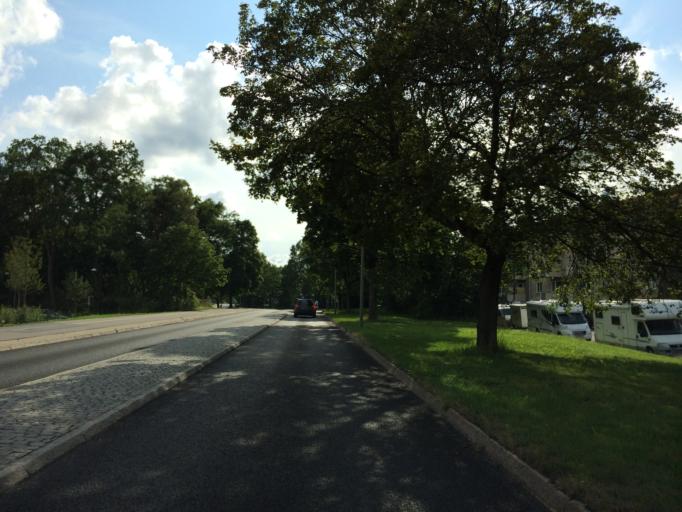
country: SE
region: Stockholm
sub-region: Huddinge Kommun
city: Segeltorp
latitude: 59.2826
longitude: 17.9672
